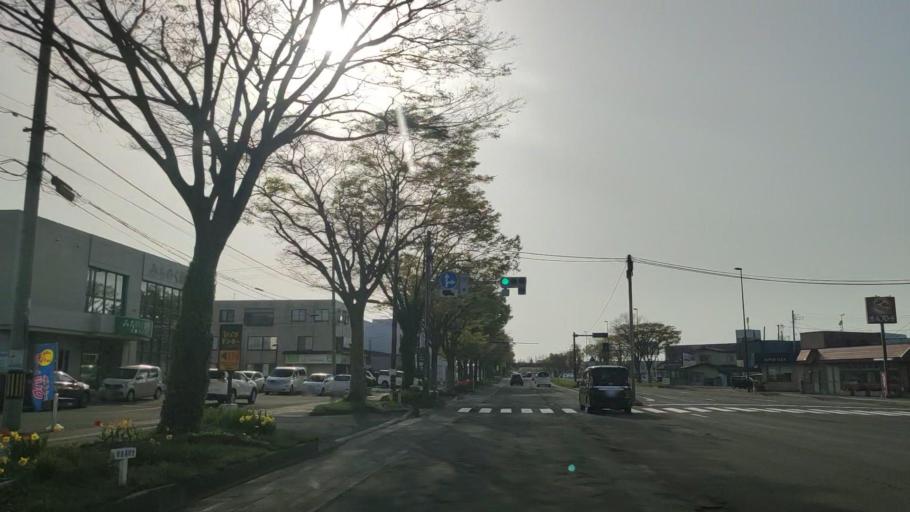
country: JP
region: Aomori
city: Aomori Shi
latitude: 40.8271
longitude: 140.7948
